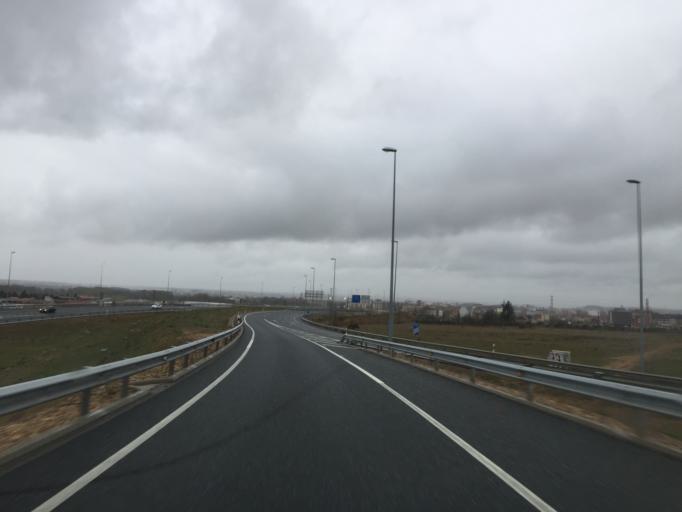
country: ES
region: Castille and Leon
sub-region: Provincia de Leon
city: Leon
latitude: 42.5714
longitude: -5.5461
